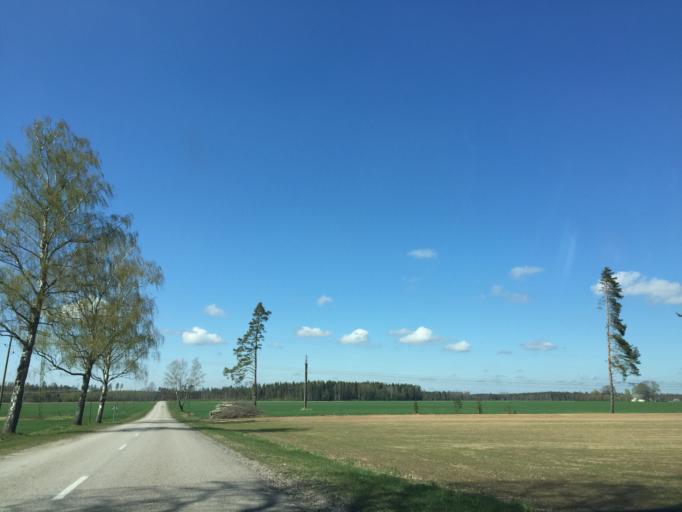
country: LV
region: Strenci
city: Seda
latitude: 57.5774
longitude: 25.7635
